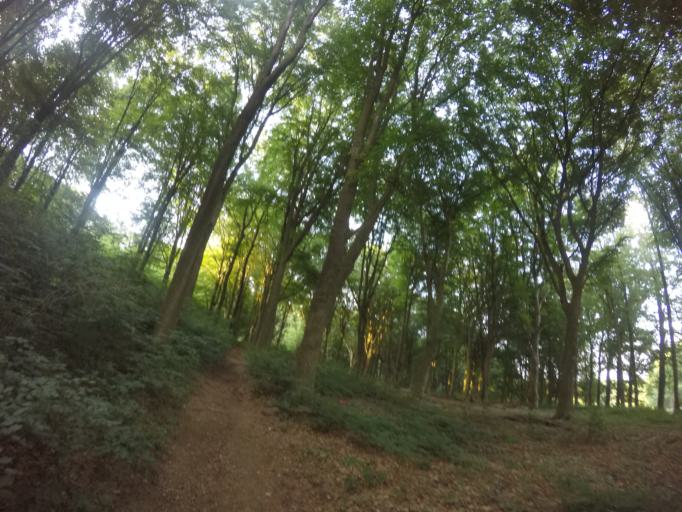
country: NL
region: Gelderland
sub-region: Gemeente Arnhem
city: Hoogkamp
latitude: 51.9877
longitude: 5.8686
